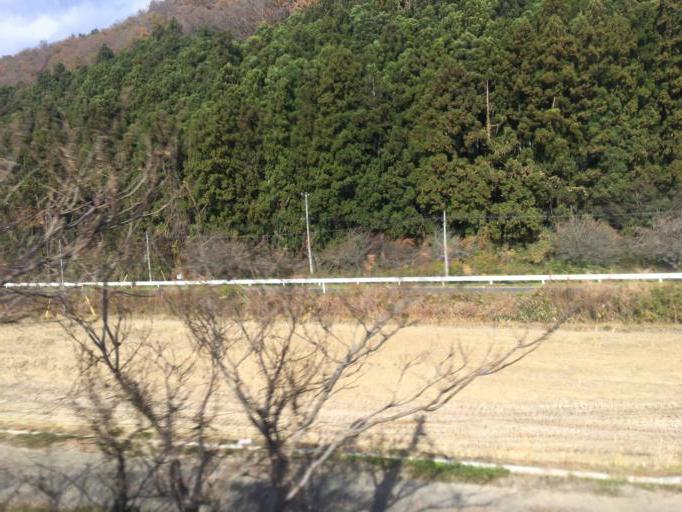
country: JP
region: Miyagi
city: Iwanuma
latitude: 38.0891
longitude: 140.8391
